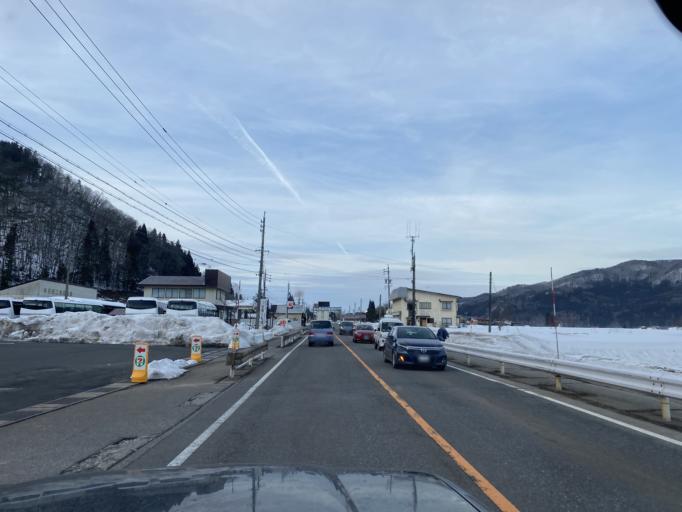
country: JP
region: Nagano
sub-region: Kitaazumi Gun
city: Hakuba
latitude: 36.6503
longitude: 137.8457
